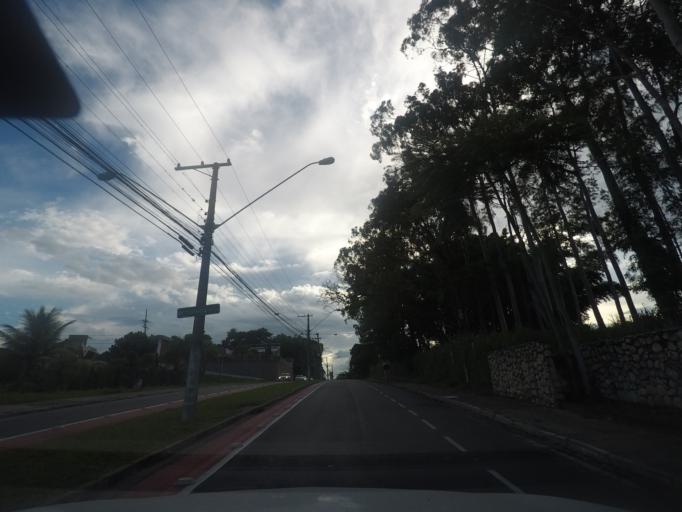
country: BR
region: Sao Paulo
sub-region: Taubate
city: Taubate
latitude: -23.0427
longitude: -45.5923
